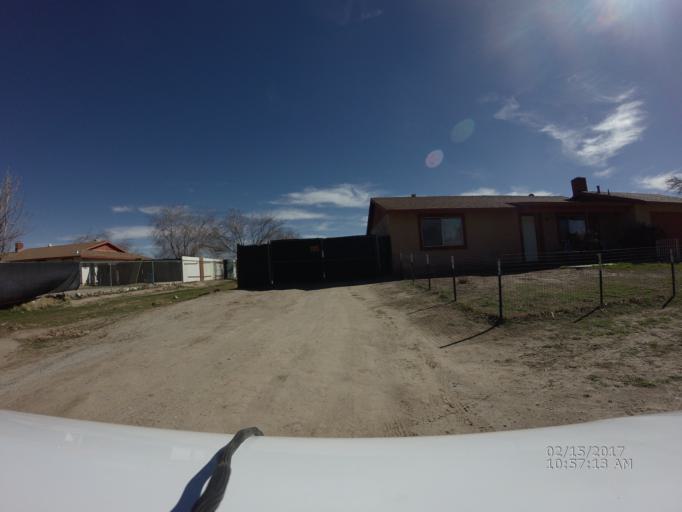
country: US
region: California
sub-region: Los Angeles County
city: Lake Los Angeles
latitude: 34.5835
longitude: -117.8517
